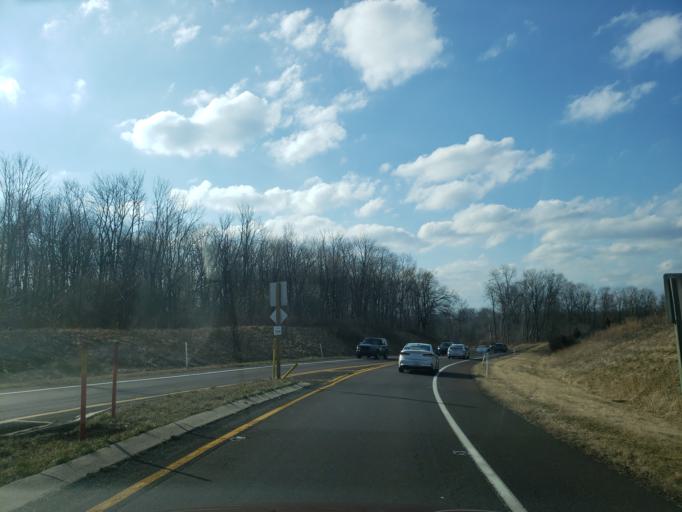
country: US
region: Pennsylvania
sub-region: Bucks County
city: New Britain
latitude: 40.2831
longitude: -75.1690
